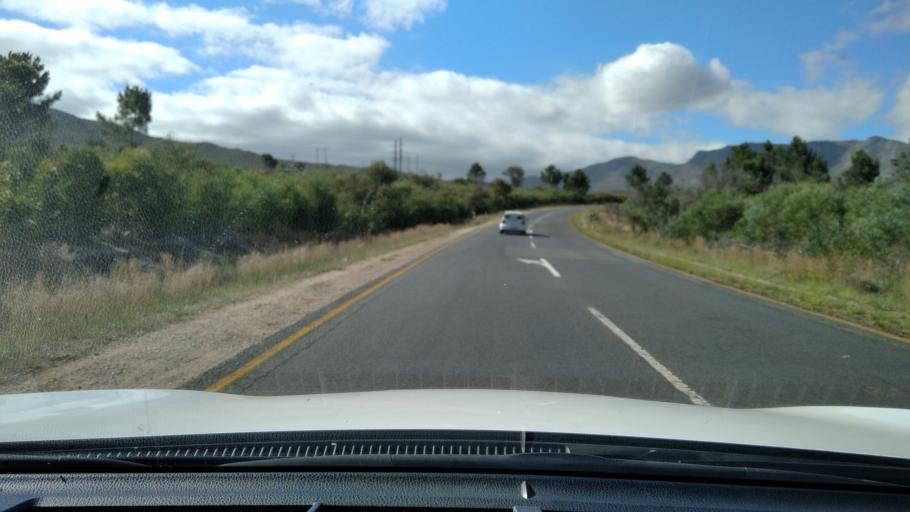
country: ZA
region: Western Cape
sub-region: Overberg District Municipality
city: Hermanus
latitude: -34.2444
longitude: 19.1855
